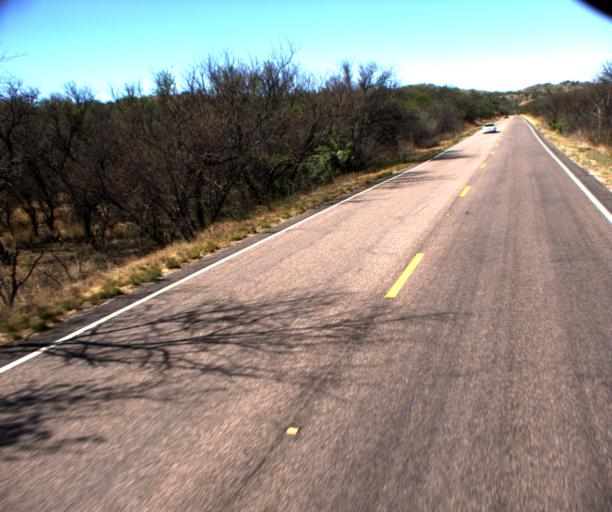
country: US
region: Arizona
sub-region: Santa Cruz County
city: Rio Rico
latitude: 31.5215
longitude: -110.7768
